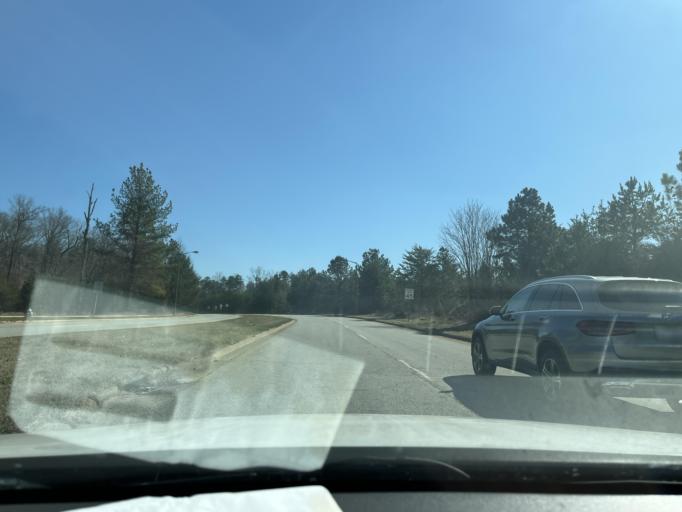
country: US
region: North Carolina
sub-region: Guilford County
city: Jamestown
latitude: 35.9956
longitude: -79.9056
